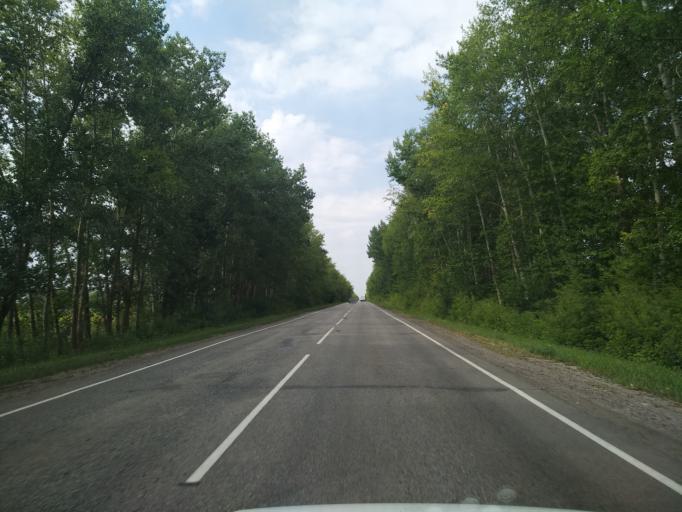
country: RU
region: Voronezj
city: Verkhnyaya Khava
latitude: 51.7105
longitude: 39.9983
